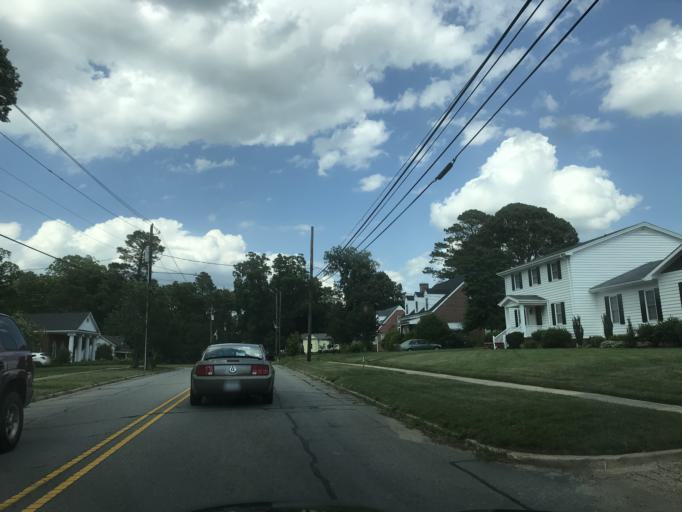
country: US
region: North Carolina
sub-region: Nash County
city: Spring Hope
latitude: 35.9462
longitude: -78.1108
